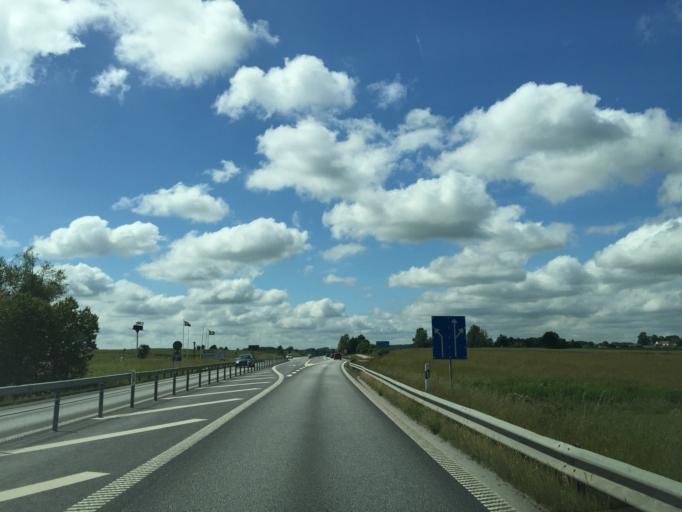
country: SE
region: Skane
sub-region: Skurups Kommun
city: Rydsgard
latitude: 55.4876
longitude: 13.5531
